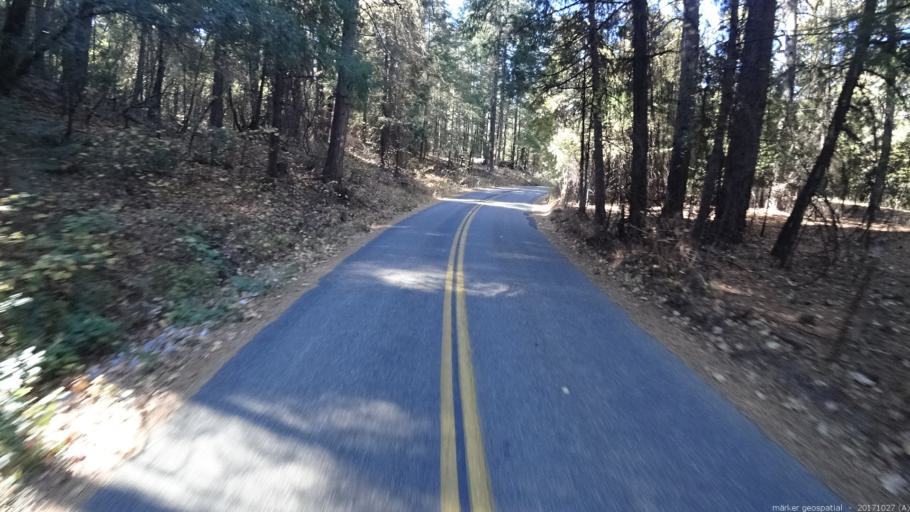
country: US
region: California
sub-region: Shasta County
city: Shingletown
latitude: 40.7386
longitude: -121.9534
